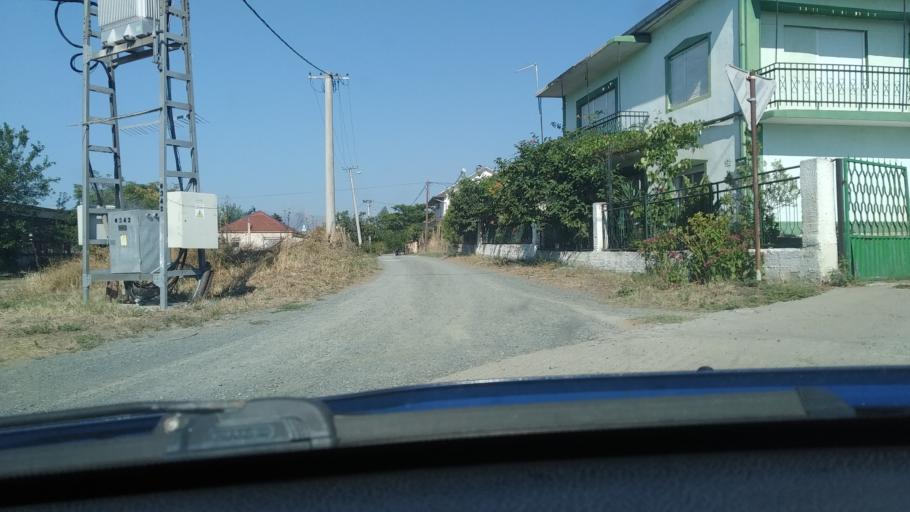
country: MK
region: Bogdanci
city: Bogdanci
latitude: 41.2045
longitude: 22.5852
